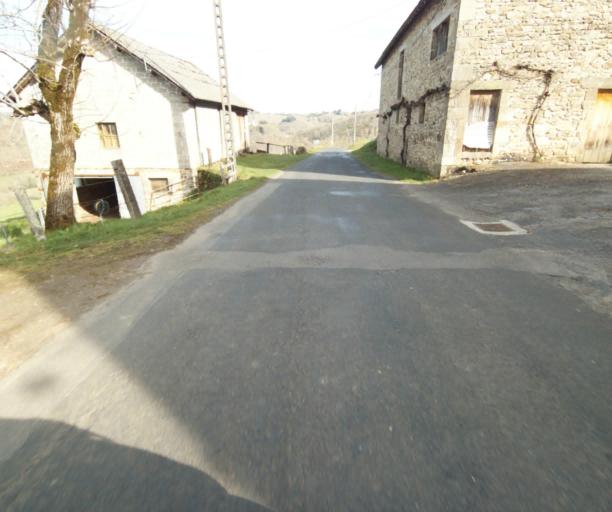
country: FR
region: Limousin
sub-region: Departement de la Correze
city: Naves
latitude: 45.3357
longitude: 1.8234
